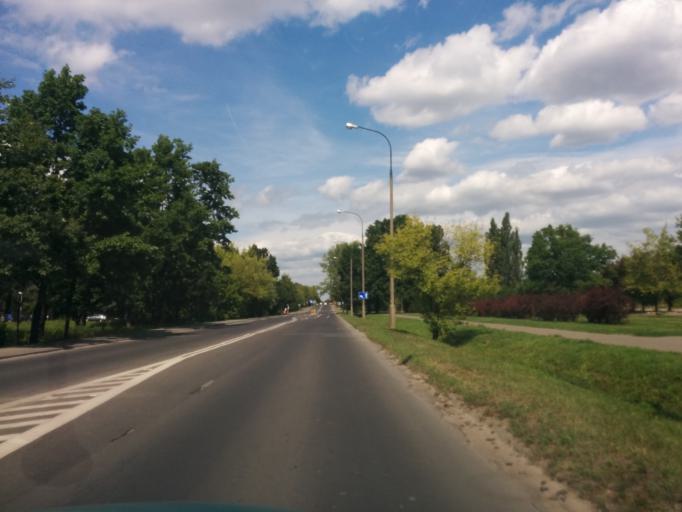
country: PL
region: Masovian Voivodeship
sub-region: Warszawa
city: Bialoleka
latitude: 52.3178
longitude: 20.9984
